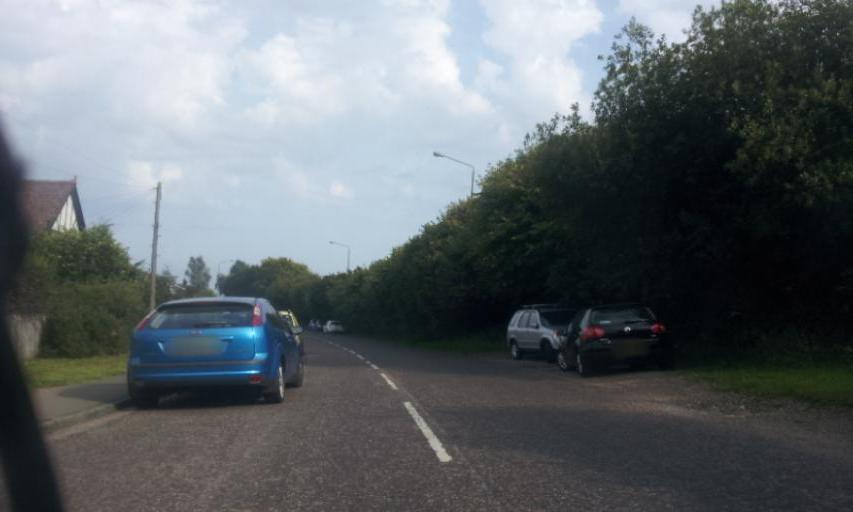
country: GB
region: England
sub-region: Kent
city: Pembury
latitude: 51.1404
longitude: 0.3301
